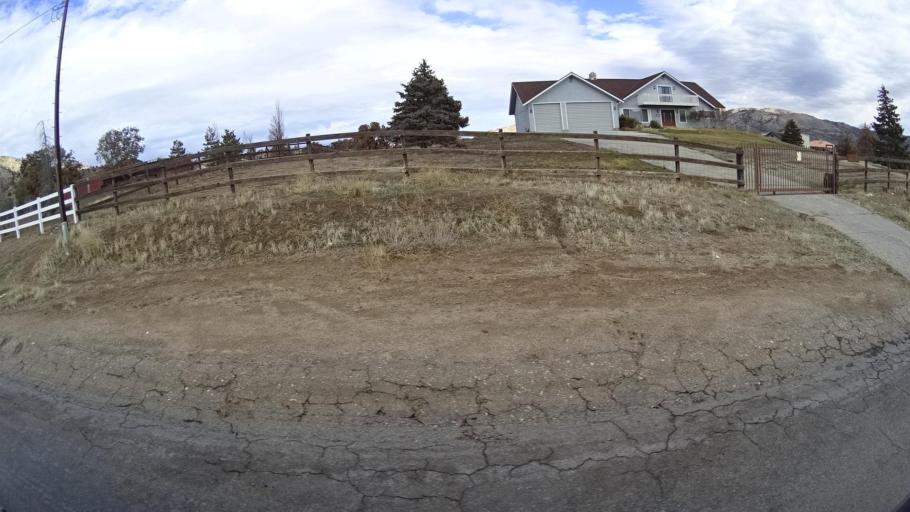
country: US
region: California
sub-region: Kern County
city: Golden Hills
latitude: 35.1542
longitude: -118.5061
